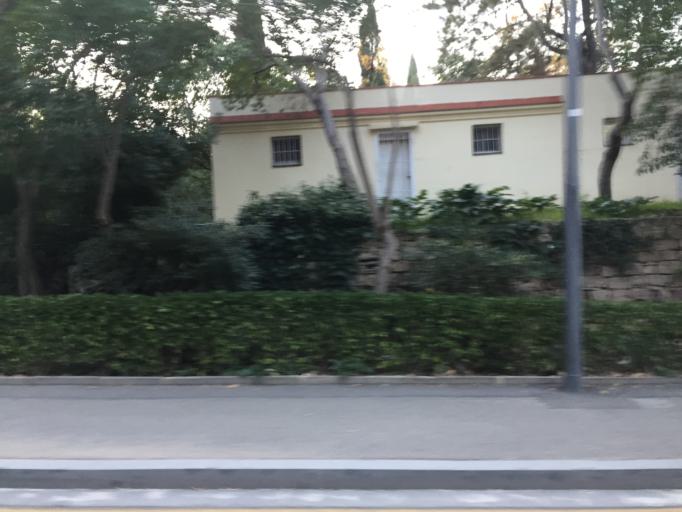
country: ES
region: Catalonia
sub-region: Provincia de Barcelona
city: Sants-Montjuic
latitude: 41.3688
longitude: 2.1583
